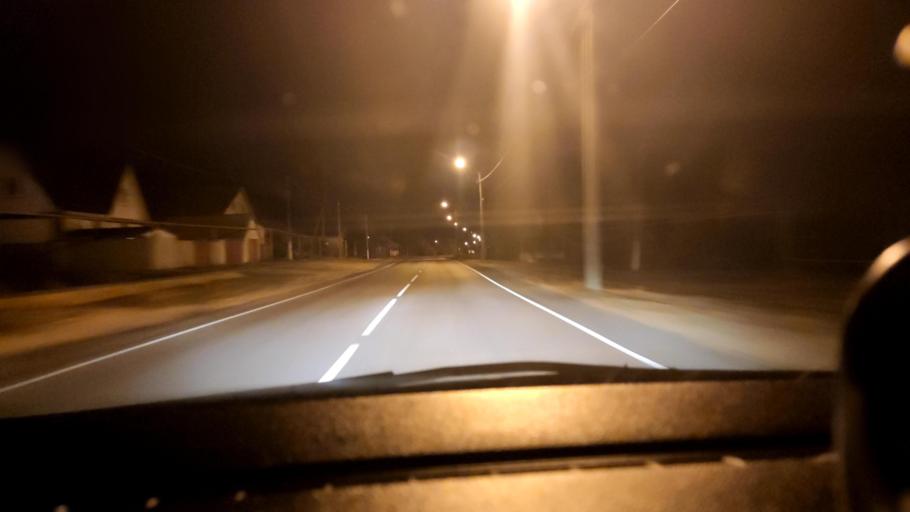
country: RU
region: Voronezj
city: Shilovo
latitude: 51.5695
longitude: 39.0454
